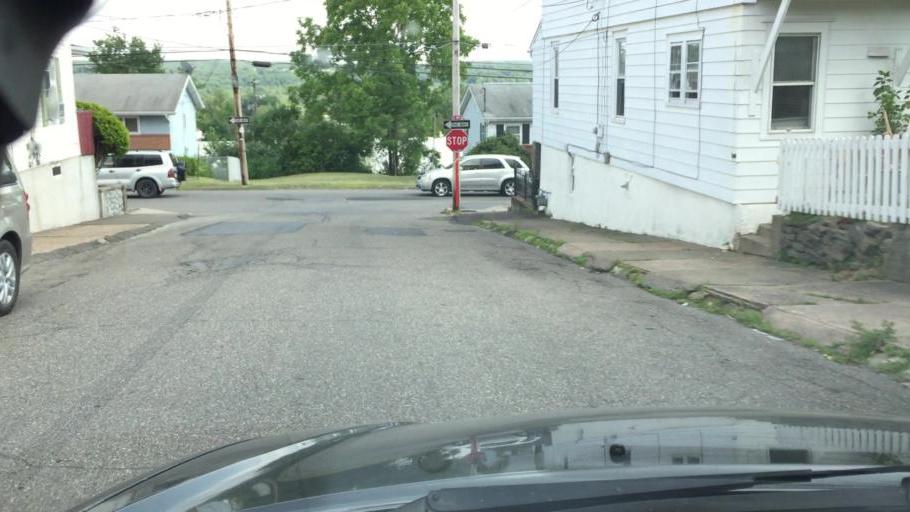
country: US
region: Pennsylvania
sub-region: Luzerne County
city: West Hazleton
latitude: 40.9579
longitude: -75.9986
